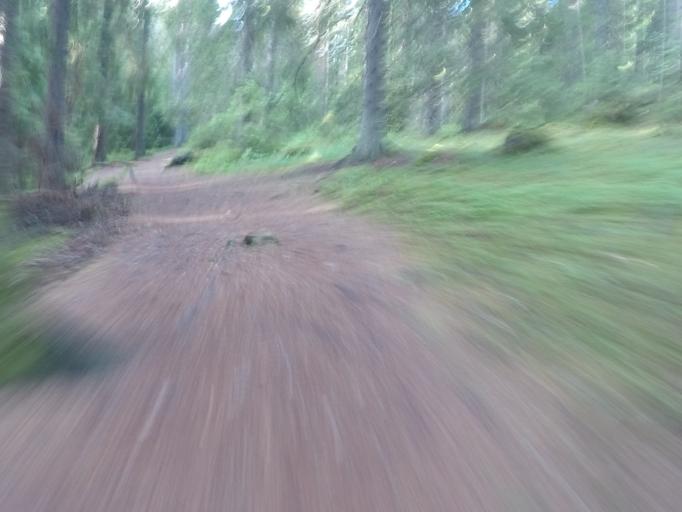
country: SE
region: Soedermanland
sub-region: Eskilstuna Kommun
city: Hallbybrunn
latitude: 59.3942
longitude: 16.4043
